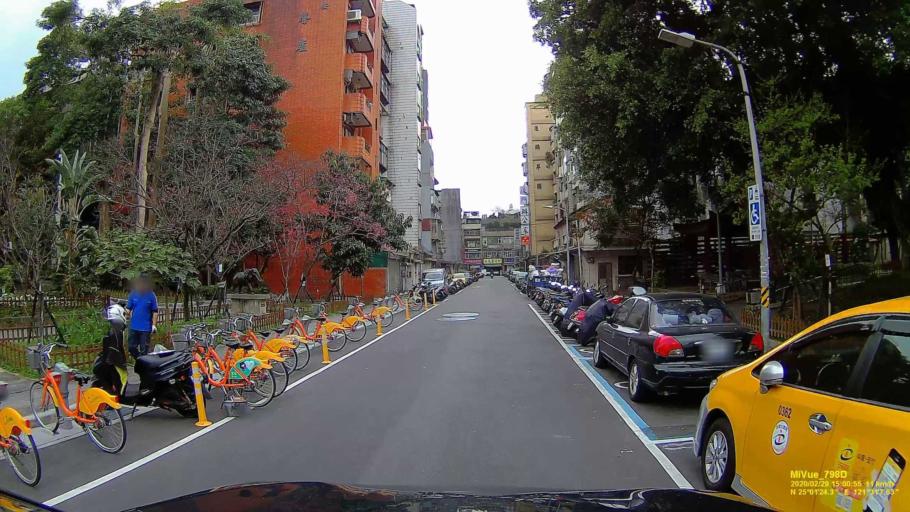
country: TW
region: Taipei
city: Taipei
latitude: 25.0234
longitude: 121.5190
